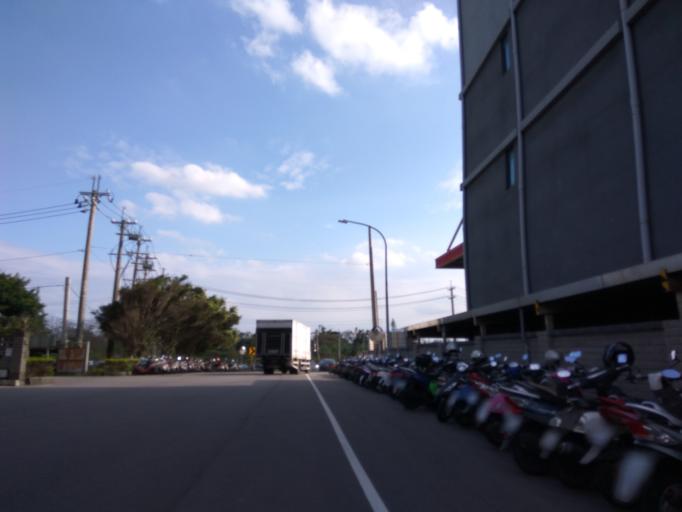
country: TW
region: Taiwan
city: Taoyuan City
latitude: 25.0483
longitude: 121.1778
